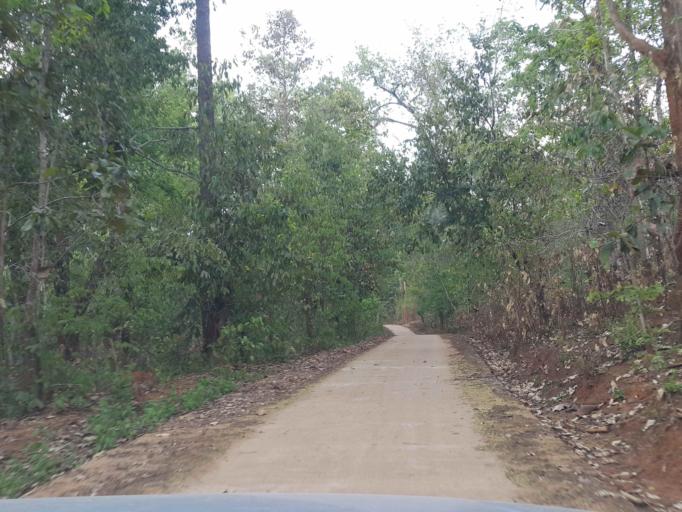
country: TH
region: Chiang Mai
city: Wiang Haeng
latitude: 19.3694
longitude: 98.7184
